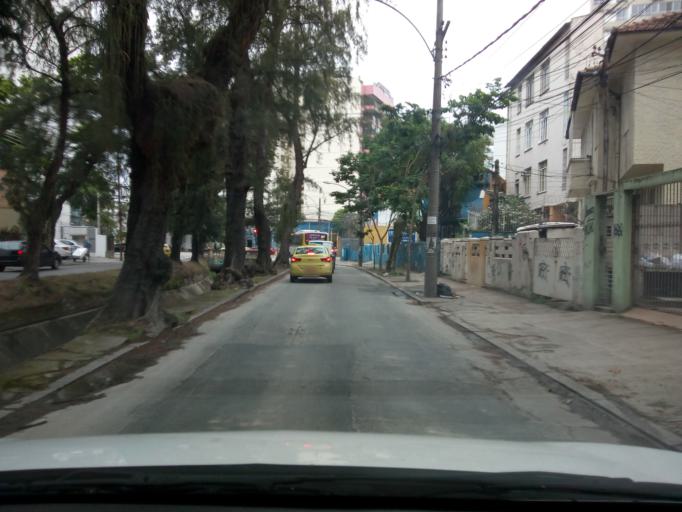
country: BR
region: Rio de Janeiro
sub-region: Rio De Janeiro
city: Rio de Janeiro
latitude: -22.9187
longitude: -43.2205
